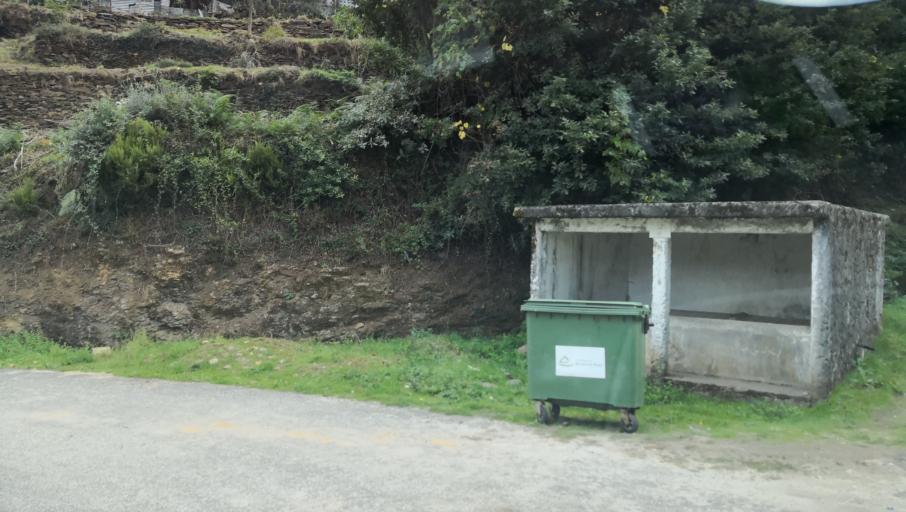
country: PT
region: Vila Real
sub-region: Mondim de Basto
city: Mondim de Basto
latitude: 41.3559
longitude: -7.8891
